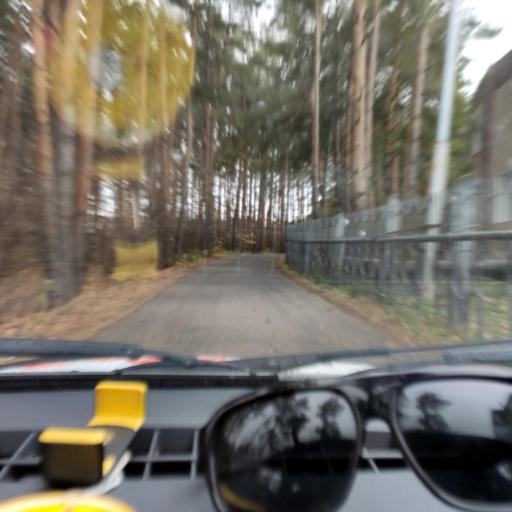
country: RU
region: Bashkortostan
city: Ufa
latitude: 54.7034
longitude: 56.0123
